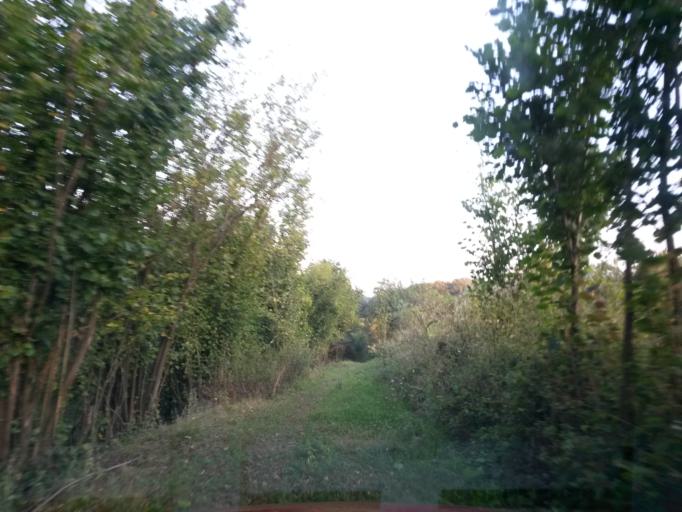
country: SK
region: Presovsky
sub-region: Okres Presov
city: Presov
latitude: 48.9113
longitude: 21.2002
